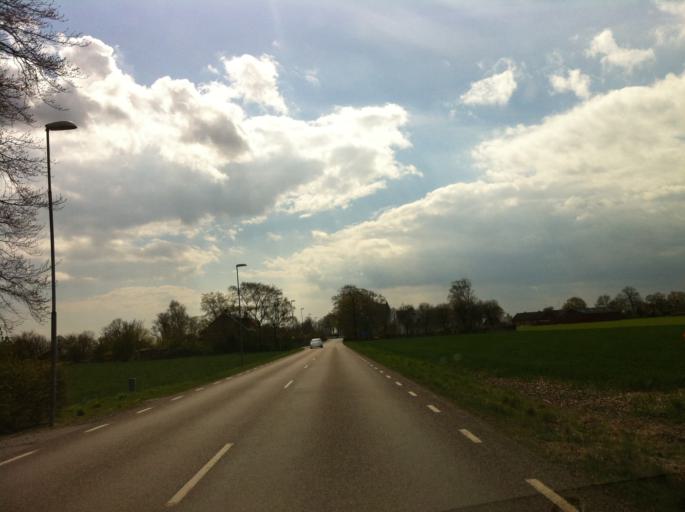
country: SE
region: Skane
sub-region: Kavlinge Kommun
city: Kaevlinge
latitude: 55.8083
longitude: 13.1587
